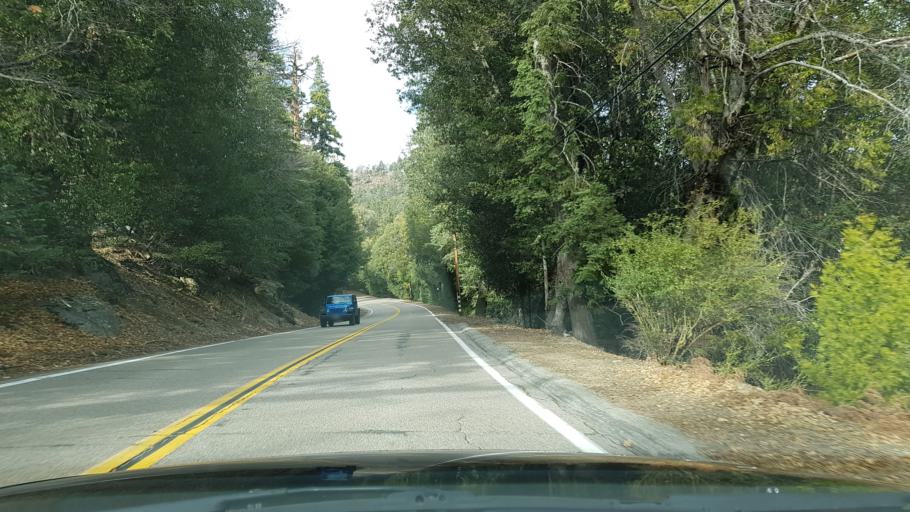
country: US
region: California
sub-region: Riverside County
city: Aguanga
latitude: 33.3371
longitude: -116.8743
